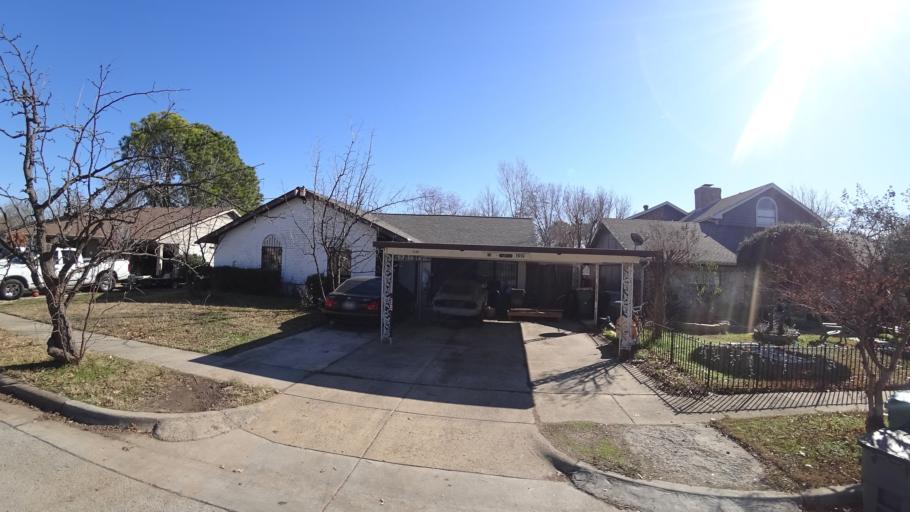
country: US
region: Texas
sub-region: Denton County
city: Lewisville
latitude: 33.0319
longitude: -97.0164
